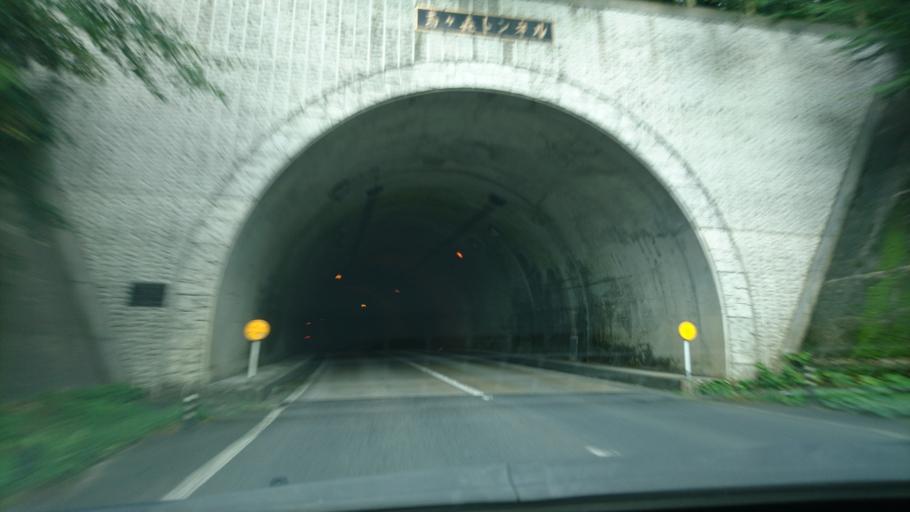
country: JP
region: Iwate
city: Mizusawa
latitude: 39.0318
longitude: 141.2638
